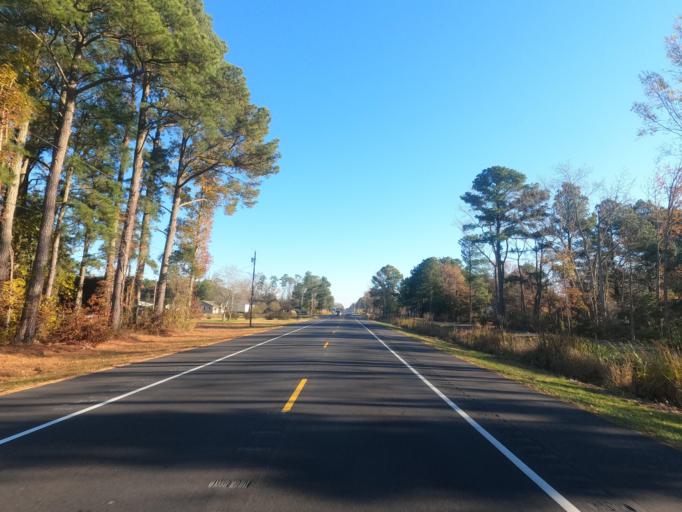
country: US
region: Maryland
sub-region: Somerset County
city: Crisfield
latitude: 38.0066
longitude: -75.8207
